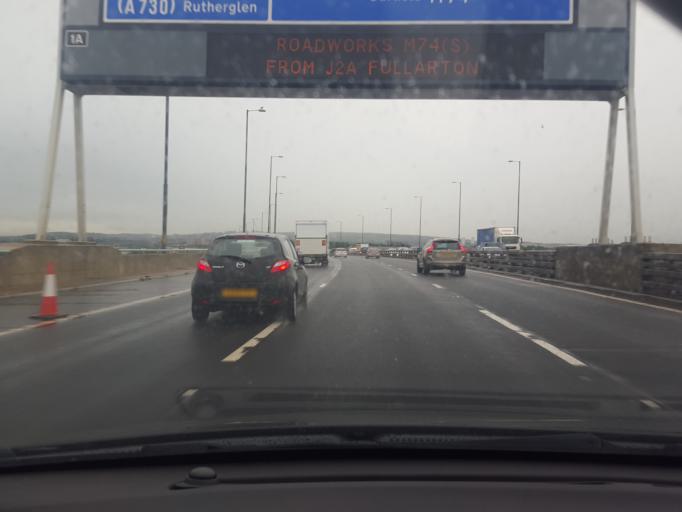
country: GB
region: Scotland
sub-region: Glasgow City
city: Glasgow
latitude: 55.8480
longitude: -4.2630
